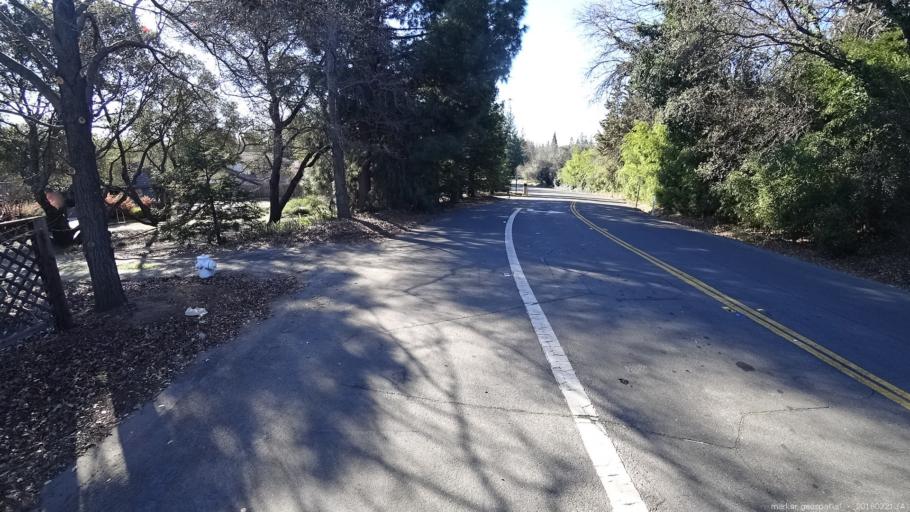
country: US
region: California
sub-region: Sacramento County
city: Orangevale
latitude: 38.6785
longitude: -121.2499
